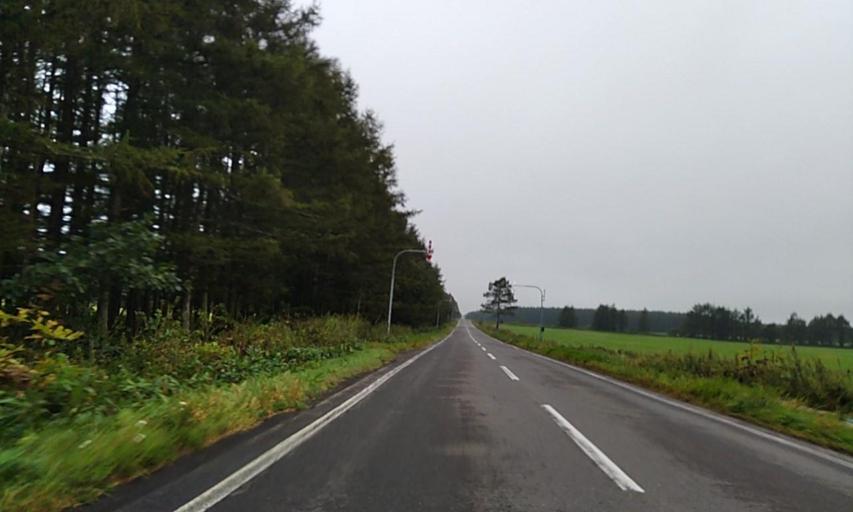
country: JP
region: Hokkaido
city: Shibetsu
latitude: 43.5253
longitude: 144.6924
